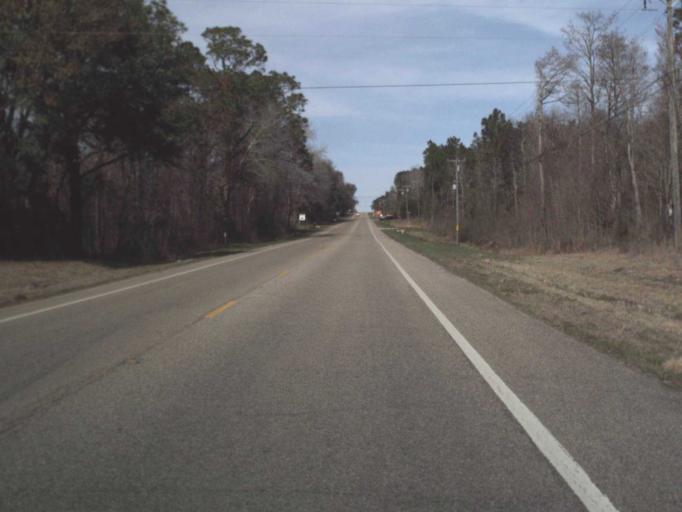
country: US
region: Florida
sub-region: Washington County
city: Chipley
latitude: 30.8575
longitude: -85.5281
